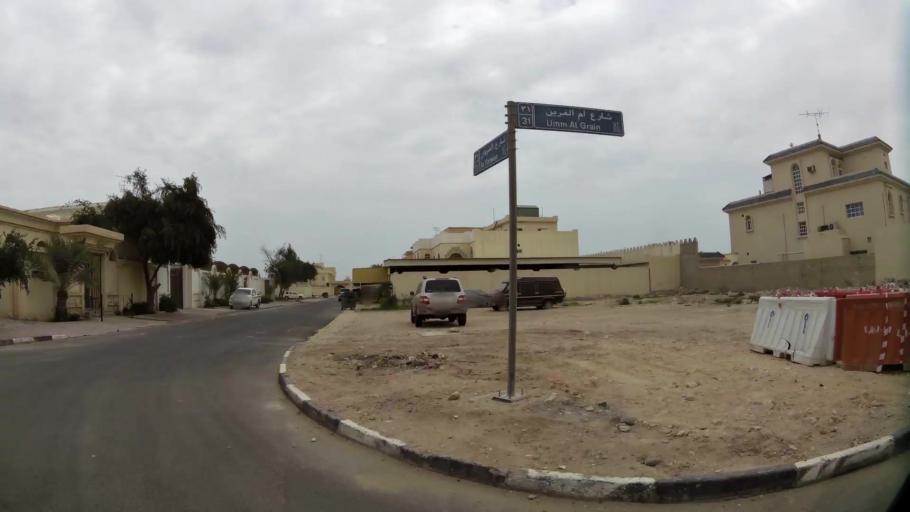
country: QA
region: Baladiyat ar Rayyan
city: Ar Rayyan
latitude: 25.3424
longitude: 51.4611
